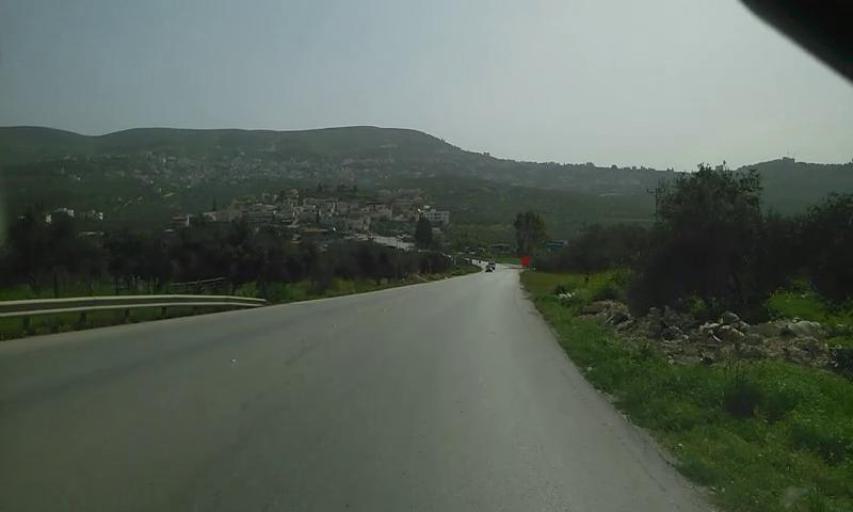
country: PS
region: West Bank
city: Al Fandaqumiyah
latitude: 32.3359
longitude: 35.2064
